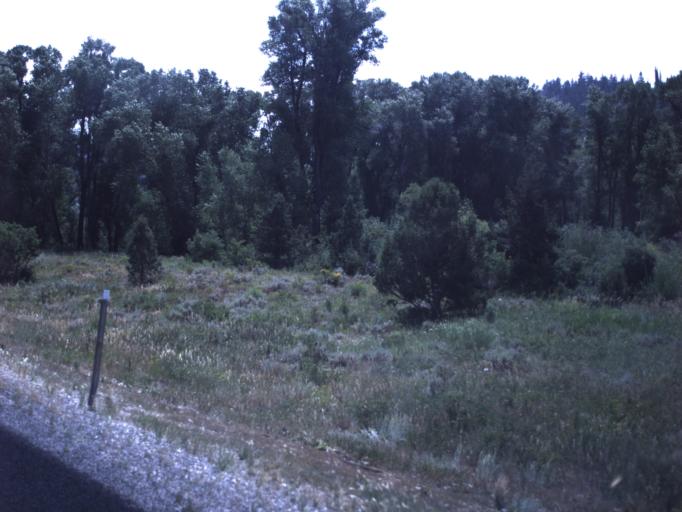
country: US
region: Utah
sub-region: Summit County
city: Francis
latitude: 40.5519
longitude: -111.1060
